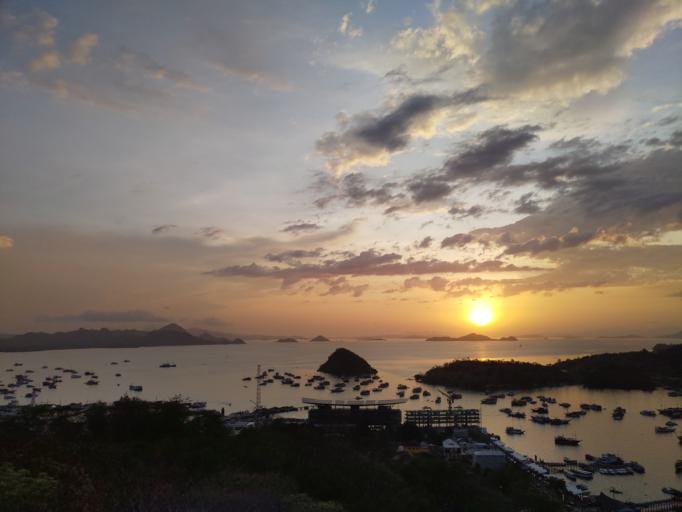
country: ID
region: East Nusa Tenggara
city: Cempa
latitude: -8.4875
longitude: 119.8797
